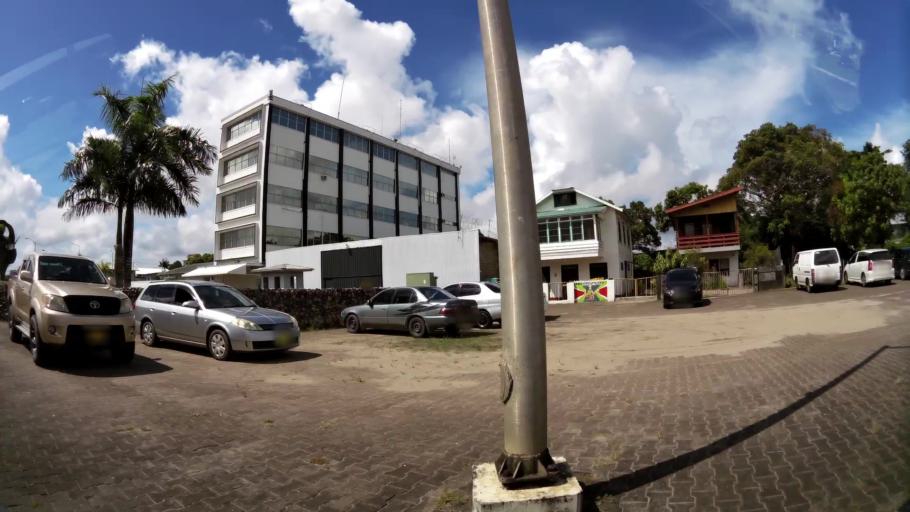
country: SR
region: Paramaribo
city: Paramaribo
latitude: 5.8282
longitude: -55.1685
